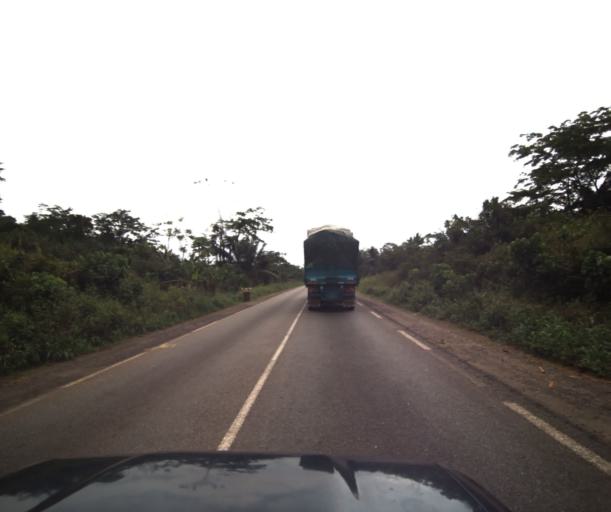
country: CM
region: Littoral
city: Edea
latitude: 3.8167
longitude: 10.3644
